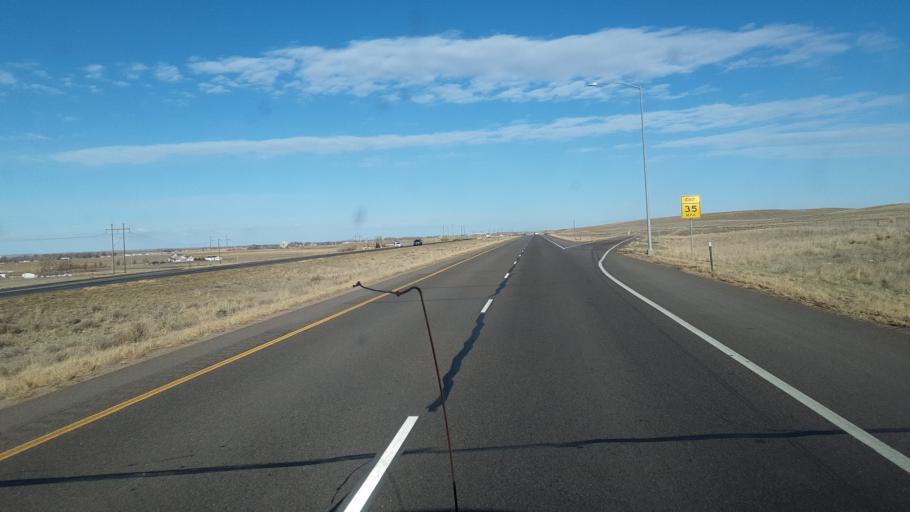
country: US
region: Colorado
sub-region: Morgan County
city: Brush
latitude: 40.2988
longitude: -103.5315
